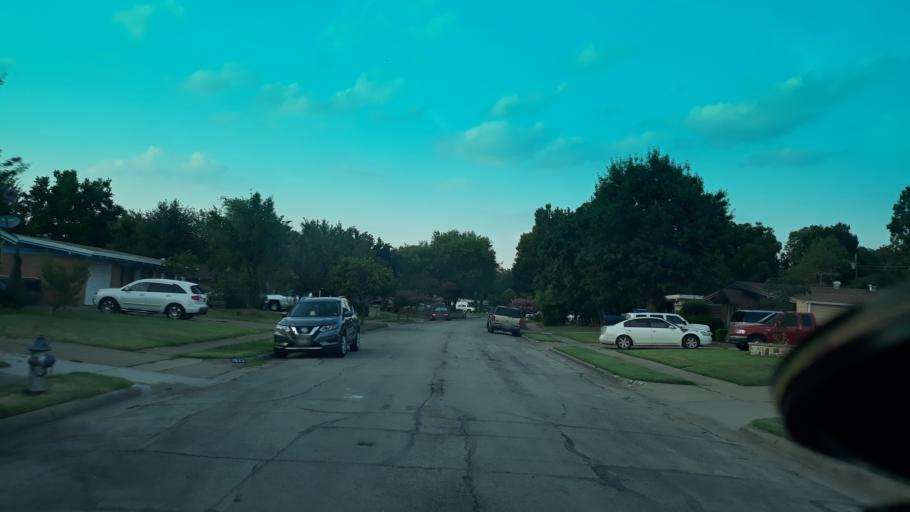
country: US
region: Texas
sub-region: Dallas County
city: Irving
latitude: 32.8331
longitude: -96.9836
